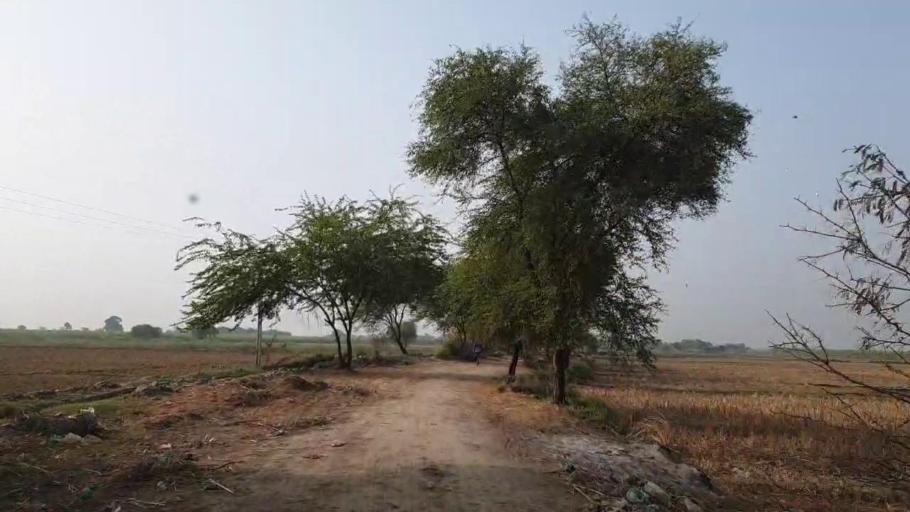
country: PK
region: Sindh
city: Matli
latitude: 25.0731
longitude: 68.6138
